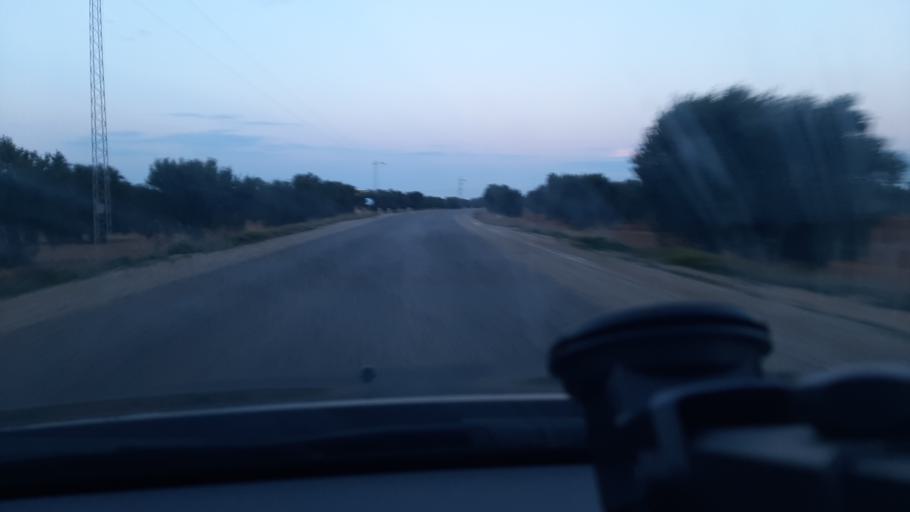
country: TN
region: Al Mahdiyah
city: Shurban
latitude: 35.0130
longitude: 10.4322
